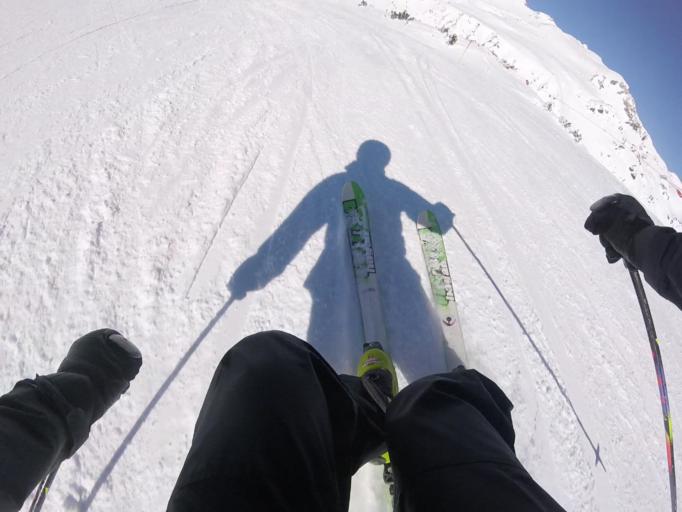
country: ES
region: Catalonia
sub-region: Provincia de Lleida
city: Espot
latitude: 42.6546
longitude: 0.9837
